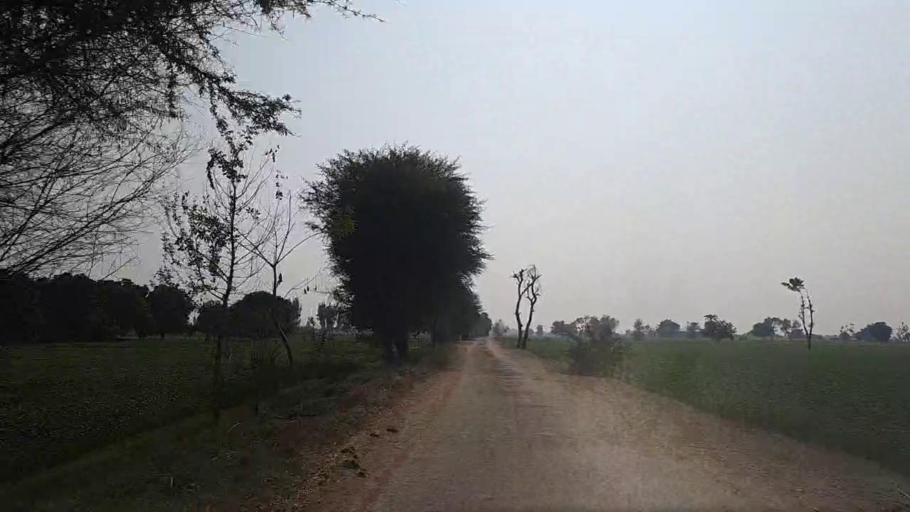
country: PK
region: Sindh
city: Jam Sahib
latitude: 26.4598
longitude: 68.5236
